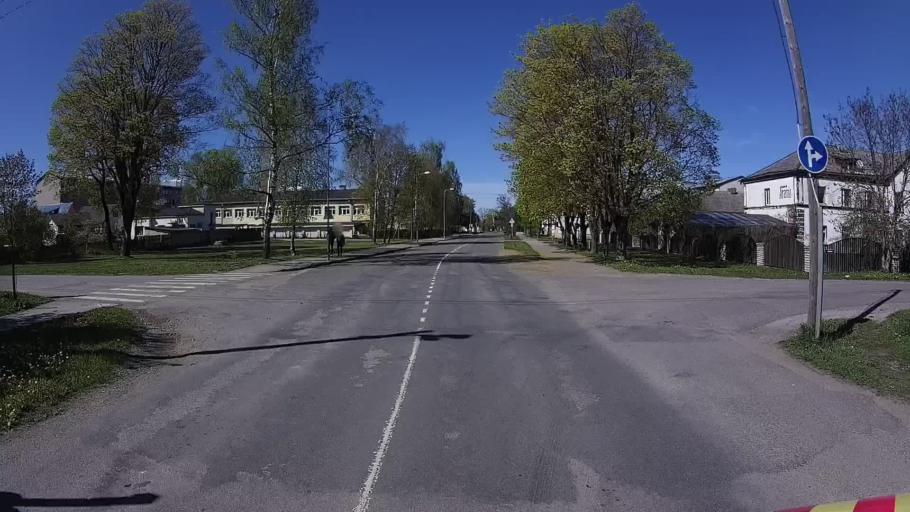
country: EE
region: Laeaene-Virumaa
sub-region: Tapa vald
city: Tapa
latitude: 59.2661
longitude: 25.9654
